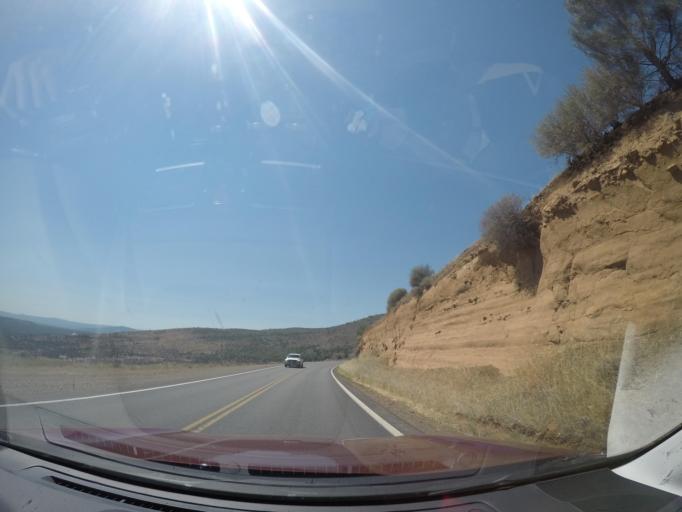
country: US
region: California
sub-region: Shasta County
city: Burney
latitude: 40.9984
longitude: -121.4982
